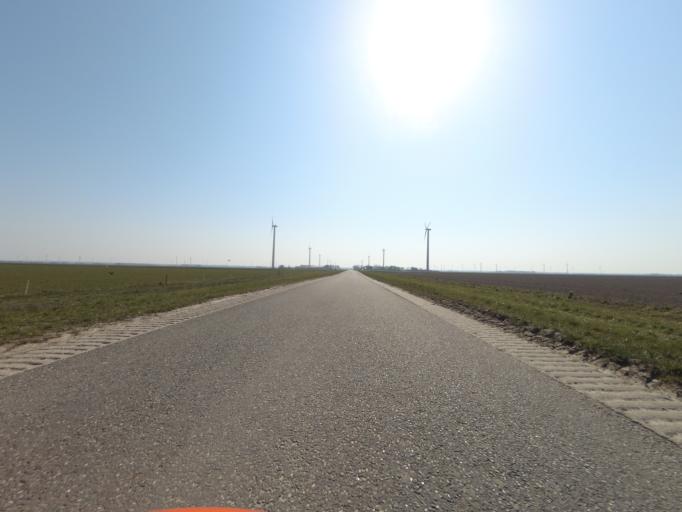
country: NL
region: Utrecht
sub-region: Gemeente Bunschoten
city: Spakenburg
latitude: 52.3495
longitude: 5.3688
